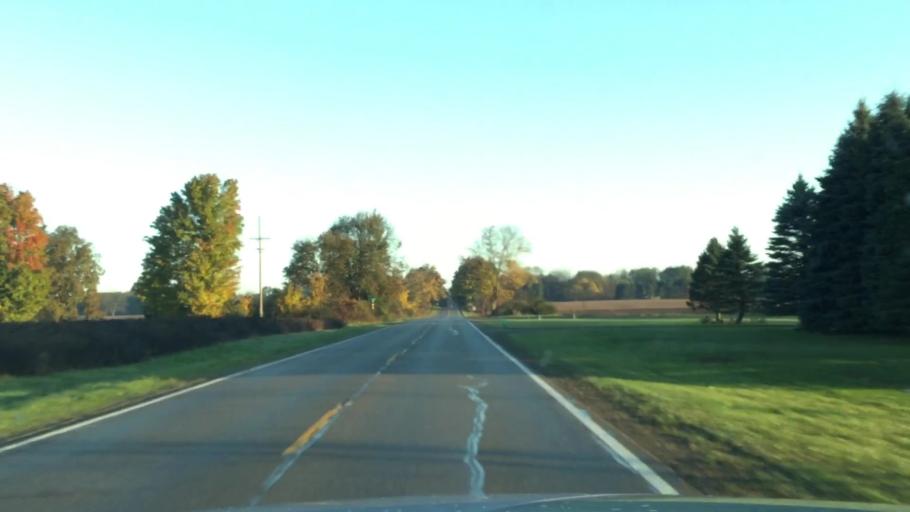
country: US
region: Michigan
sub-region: Livingston County
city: Howell
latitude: 42.7188
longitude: -83.9485
